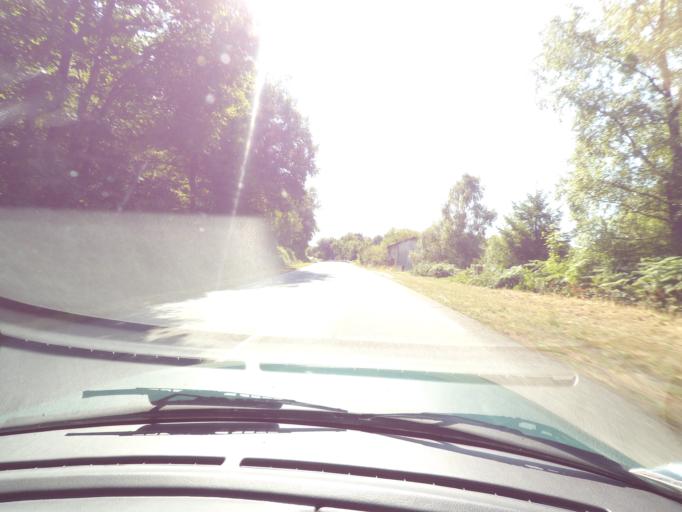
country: FR
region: Limousin
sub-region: Departement de la Haute-Vienne
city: Nieul
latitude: 45.9239
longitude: 1.1981
